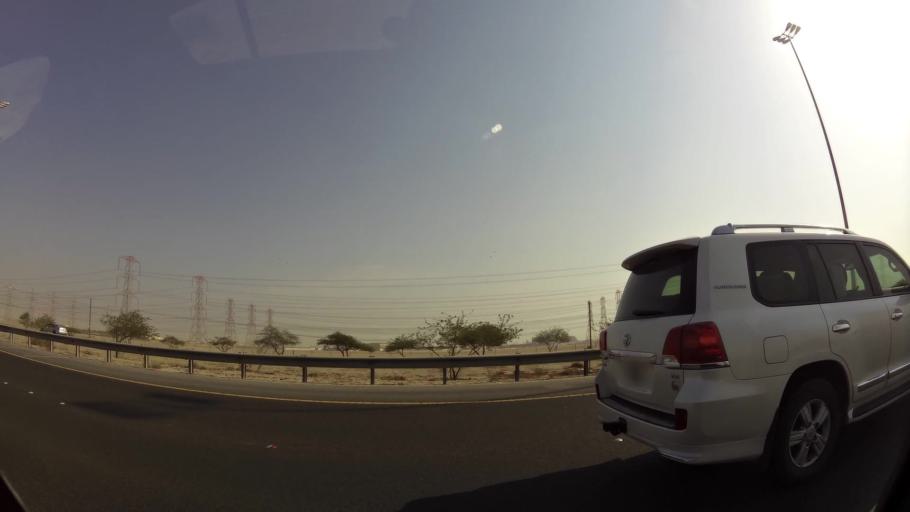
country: KW
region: Al Ahmadi
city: Al Ahmadi
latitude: 28.9843
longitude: 48.1057
